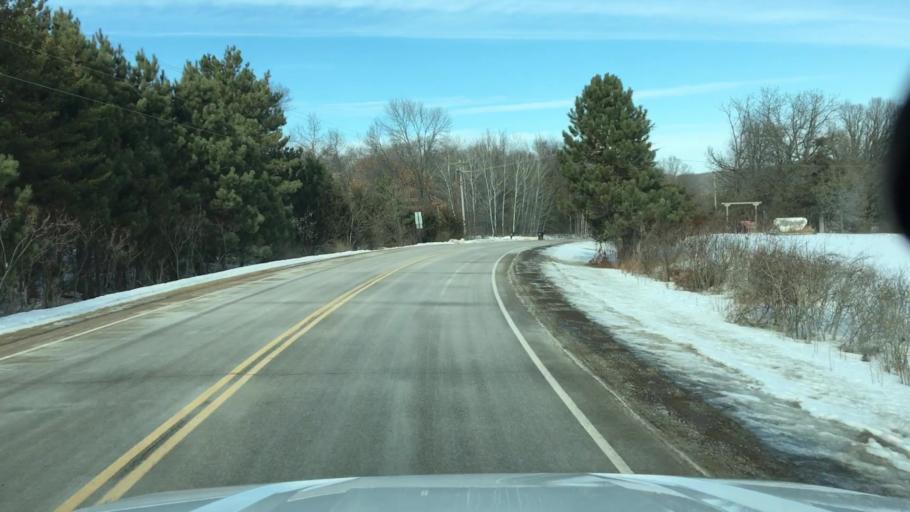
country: US
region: Wisconsin
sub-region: Polk County
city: Saint Croix Falls
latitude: 45.4525
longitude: -92.6724
